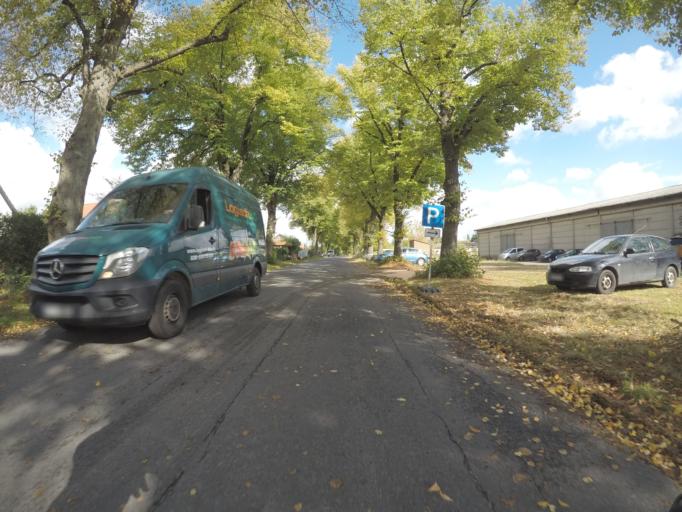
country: DE
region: Brandenburg
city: Ahrensfelde
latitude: 52.5717
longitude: 13.6182
